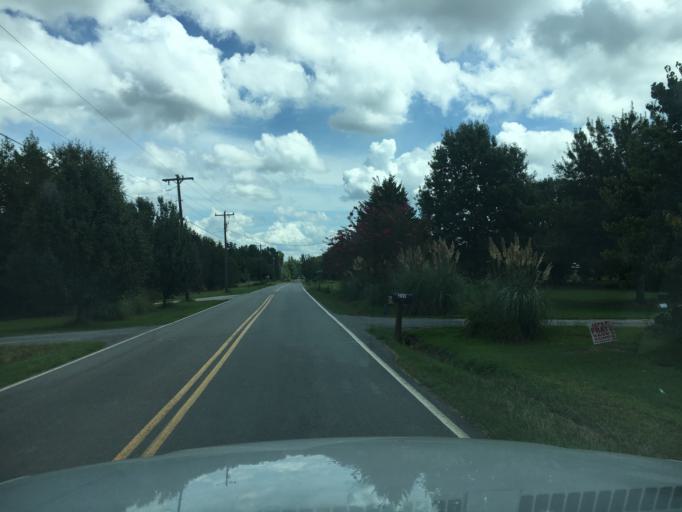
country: US
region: South Carolina
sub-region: Anderson County
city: Belton
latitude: 34.5546
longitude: -82.4668
